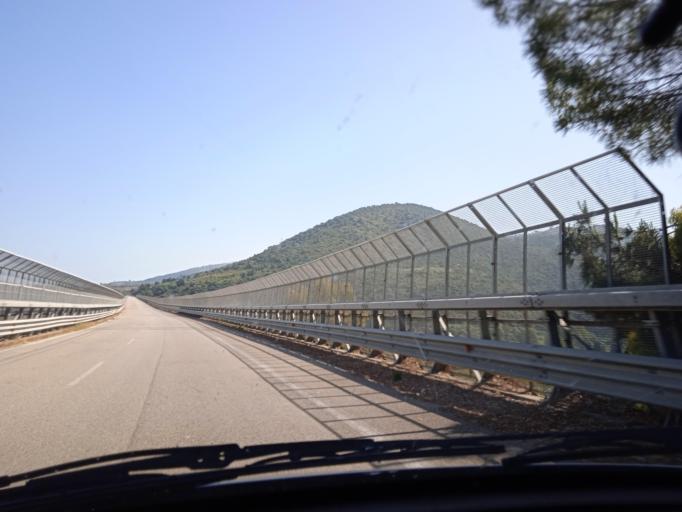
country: IT
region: Sicily
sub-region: Messina
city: Rocca di Capri Leone
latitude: 38.1052
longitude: 14.7200
